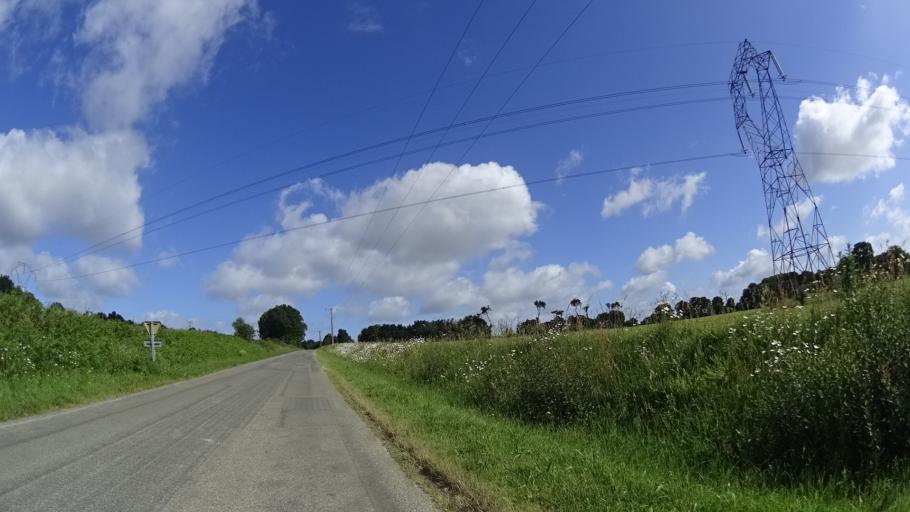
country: FR
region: Brittany
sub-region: Departement d'Ille-et-Vilaine
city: La Chapelle-des-Fougeretz
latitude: 48.1862
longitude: -1.7183
